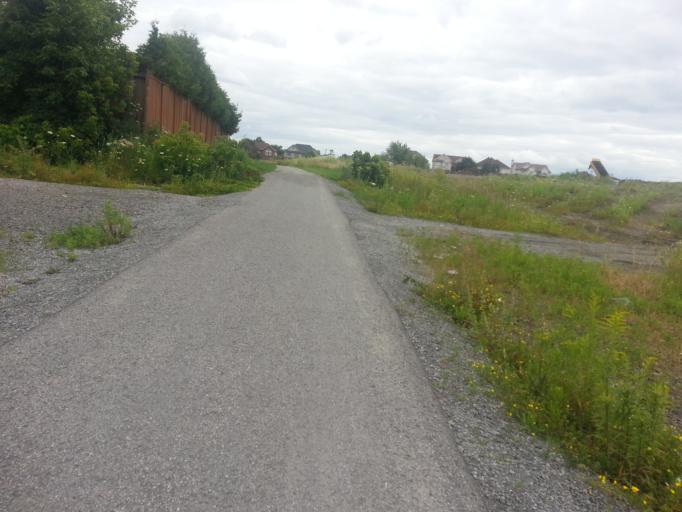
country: CA
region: Ontario
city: Bells Corners
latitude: 45.3249
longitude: -75.9290
